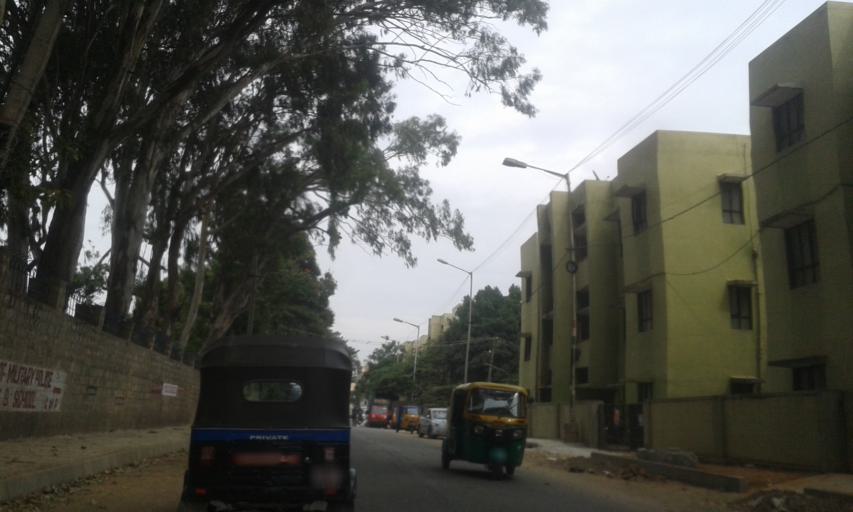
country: IN
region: Karnataka
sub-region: Bangalore Urban
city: Bangalore
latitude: 12.9596
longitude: 77.6123
